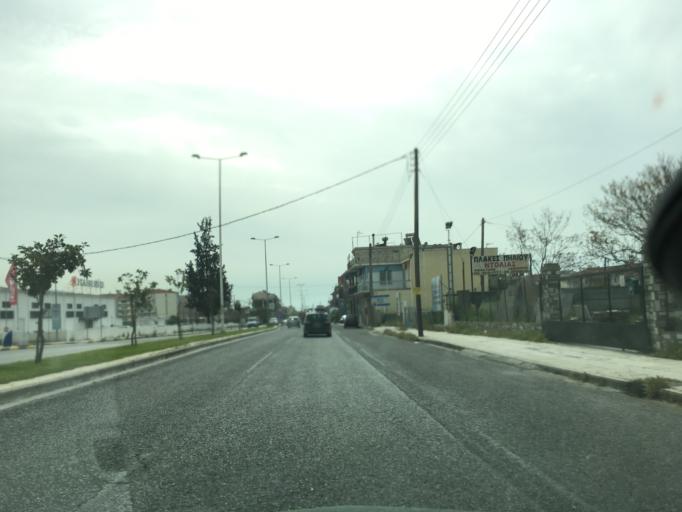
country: GR
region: Thessaly
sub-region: Nomos Magnisias
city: Nea Ionia
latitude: 39.3689
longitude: 22.9189
